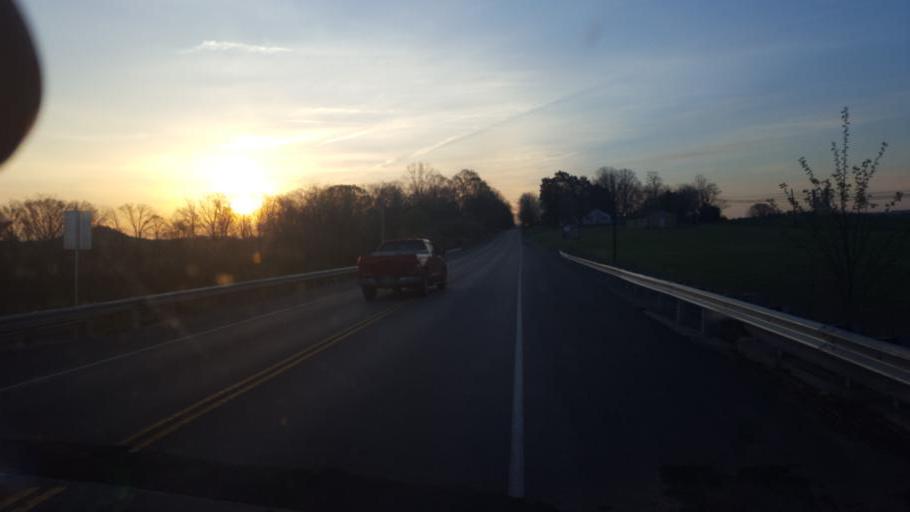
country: US
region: Kentucky
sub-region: Hart County
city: Munfordville
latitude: 37.2748
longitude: -85.9127
